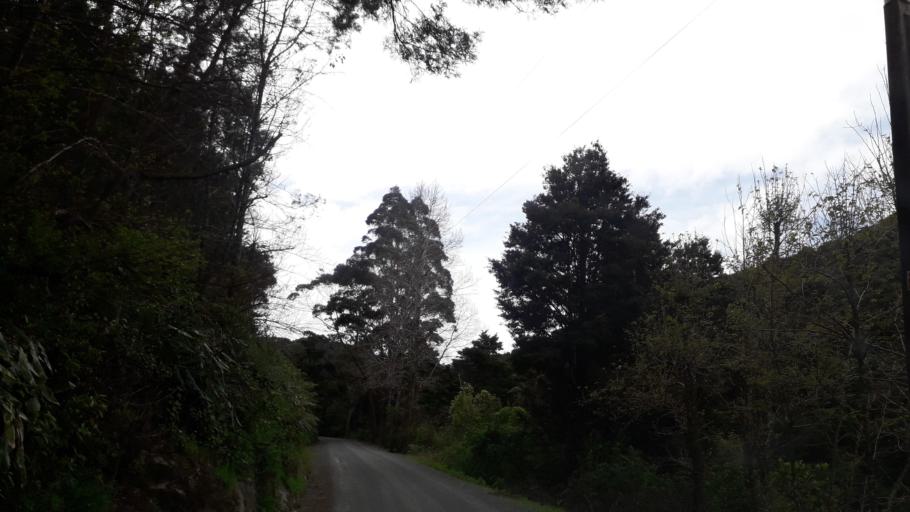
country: NZ
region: Northland
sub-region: Far North District
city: Taipa
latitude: -35.0619
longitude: 173.5503
